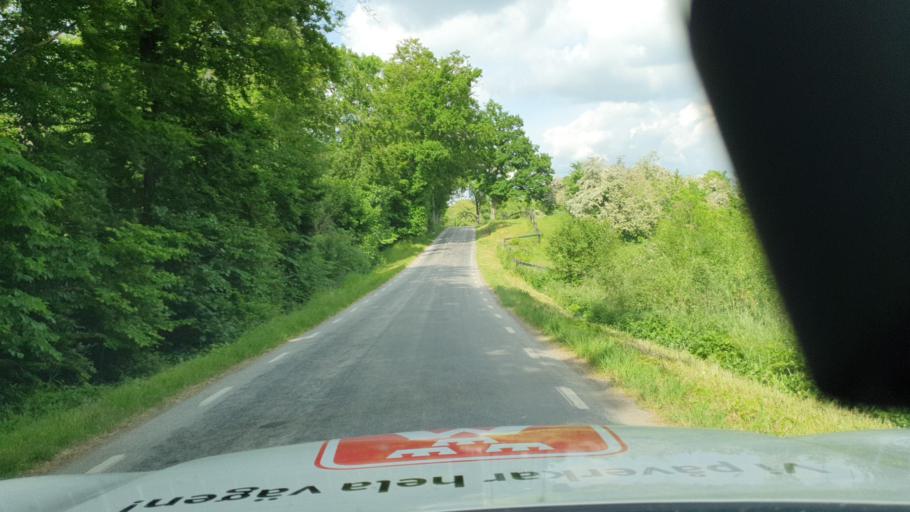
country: SE
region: Skane
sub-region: Skurups Kommun
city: Skurup
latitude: 55.5114
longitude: 13.4999
